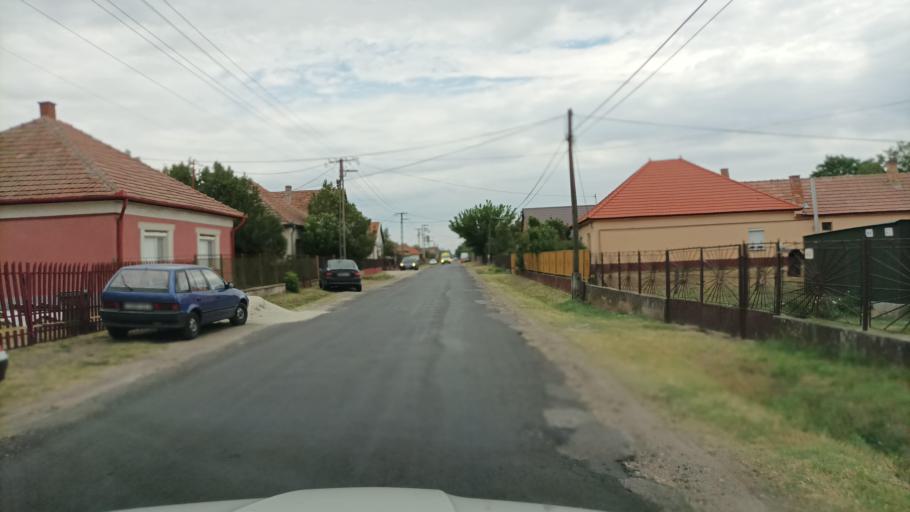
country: HU
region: Pest
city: Taborfalva
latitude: 47.1250
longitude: 19.4805
